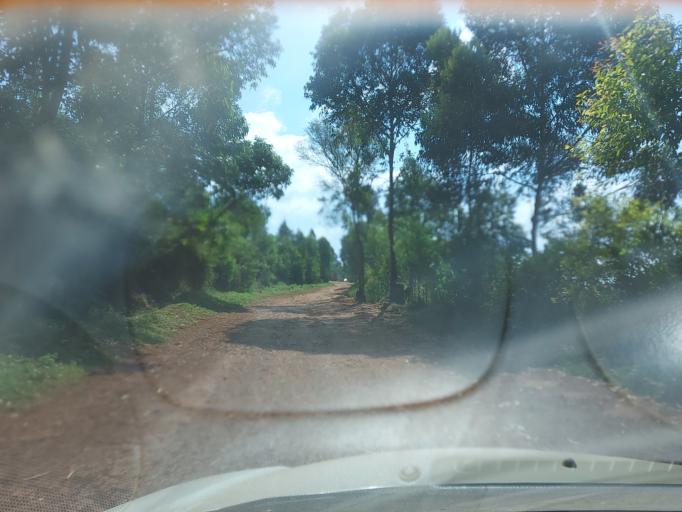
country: CD
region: South Kivu
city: Bukavu
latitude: -2.5090
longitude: 28.8325
